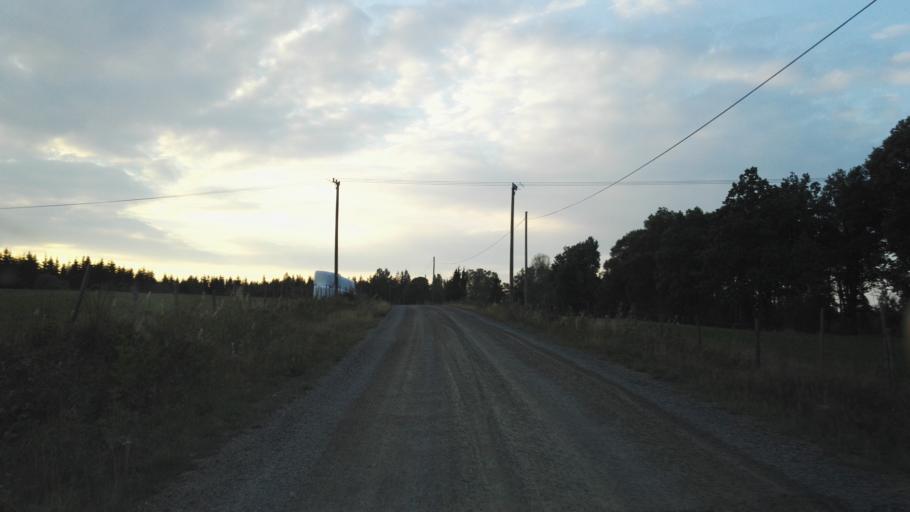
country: SE
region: Joenkoeping
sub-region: Vetlanda Kommun
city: Landsbro
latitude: 57.2205
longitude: 14.8951
